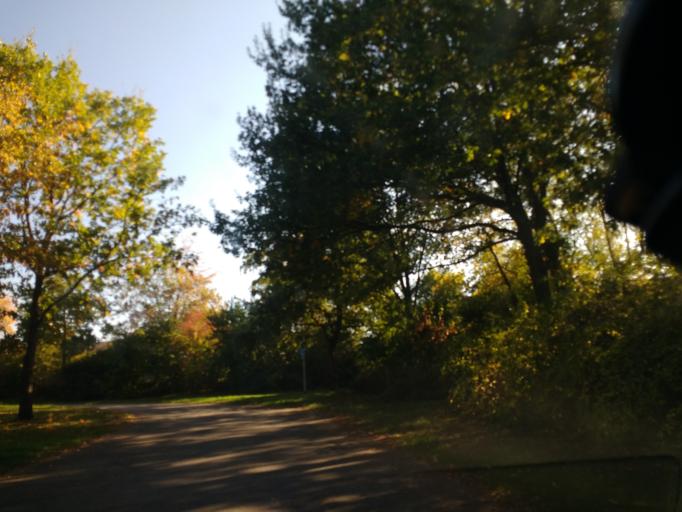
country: DE
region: Rheinland-Pfalz
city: Konz
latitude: 49.7038
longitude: 6.5964
